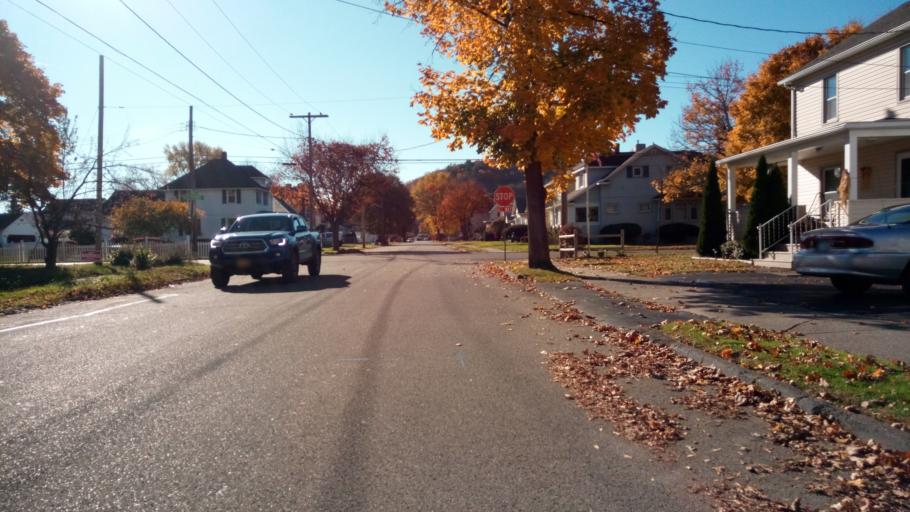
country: US
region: New York
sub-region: Chemung County
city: Southport
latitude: 42.0659
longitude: -76.8106
